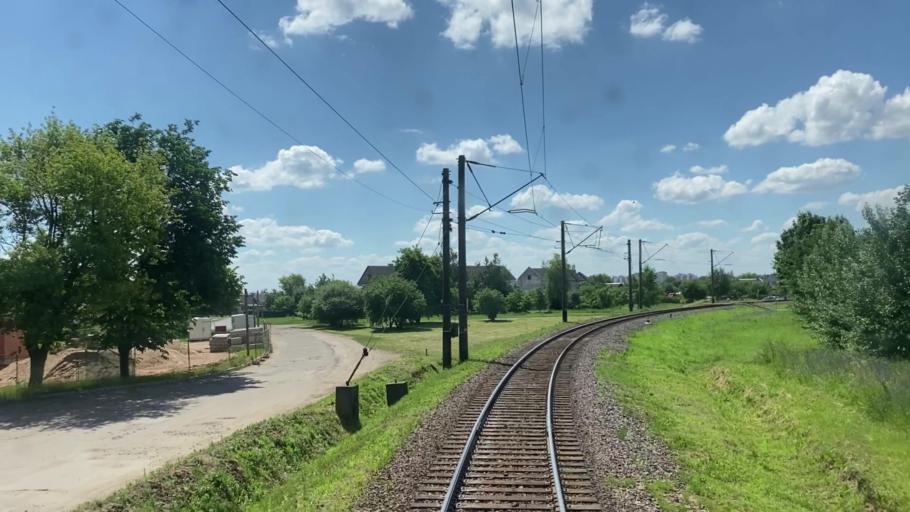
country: BY
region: Brest
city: Baranovichi
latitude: 53.1445
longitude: 26.0334
